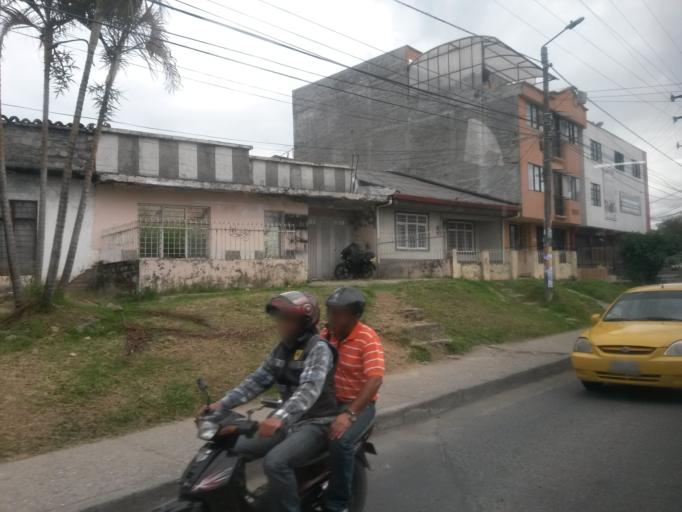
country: CO
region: Cauca
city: Popayan
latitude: 2.4532
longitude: -76.5946
